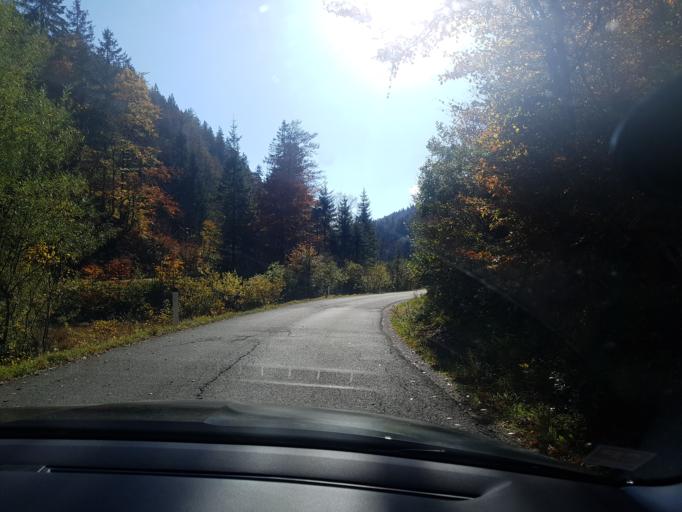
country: AT
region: Tyrol
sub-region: Politischer Bezirk Kitzbuhel
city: Hochfilzen
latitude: 47.4986
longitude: 12.6096
